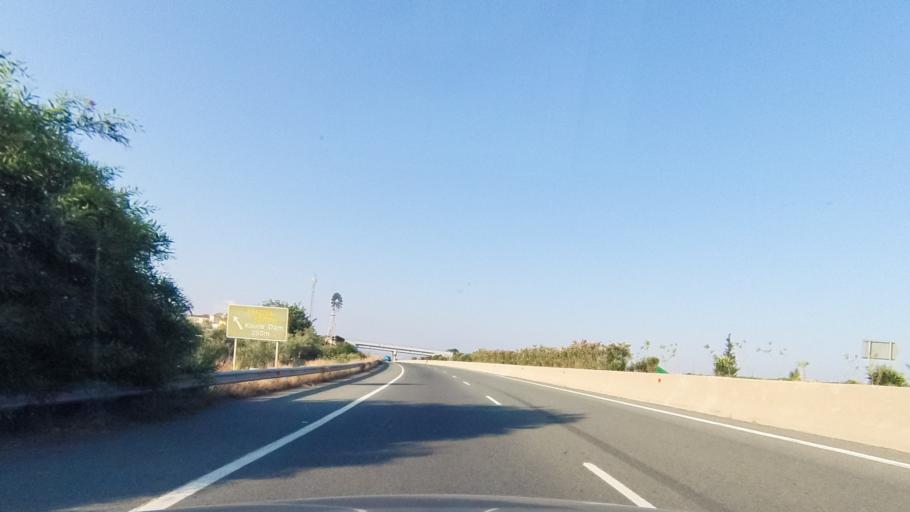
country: CY
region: Limassol
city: Ypsonas
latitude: 34.6910
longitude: 32.9430
